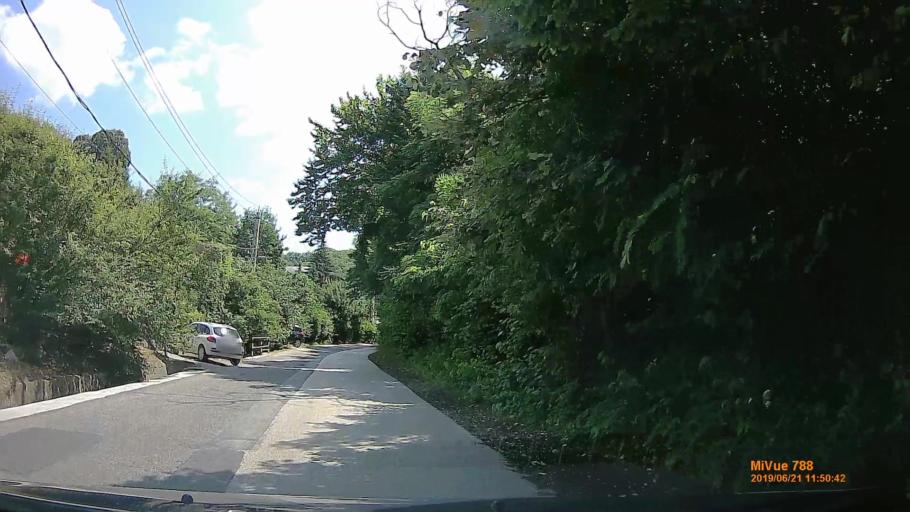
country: HU
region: Baranya
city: Pecs
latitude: 46.0920
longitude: 18.1899
